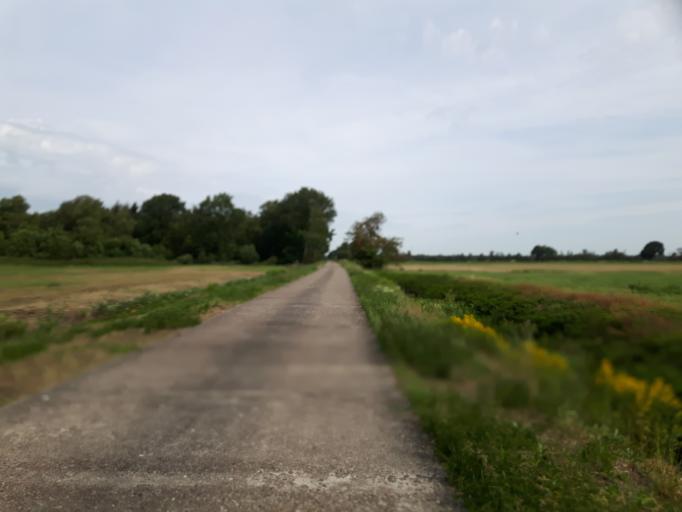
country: DE
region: Lower Saxony
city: Rastede
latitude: 53.2866
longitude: 8.2927
